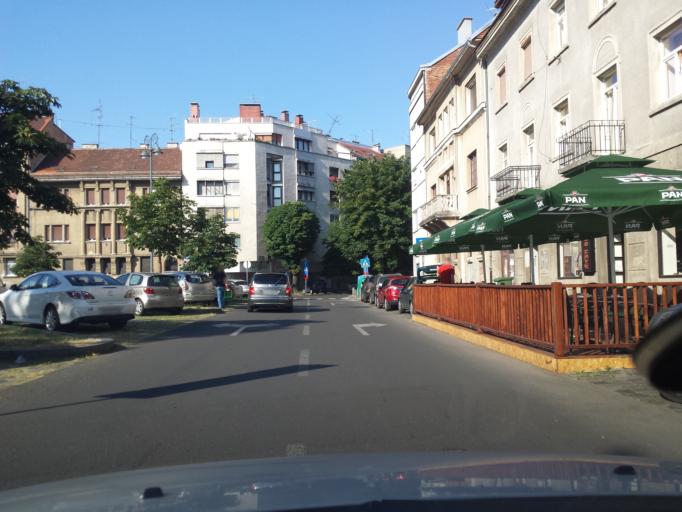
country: HR
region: Grad Zagreb
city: Zagreb - Centar
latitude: 45.8106
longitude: 15.9574
